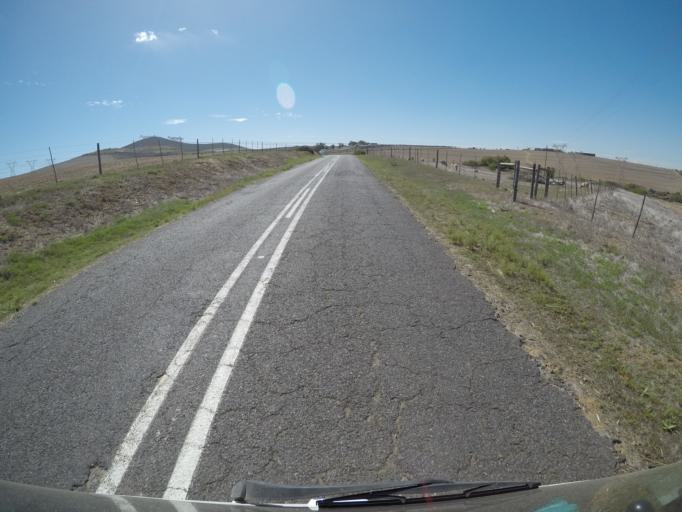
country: ZA
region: Western Cape
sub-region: City of Cape Town
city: Sunset Beach
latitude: -33.7342
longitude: 18.5657
